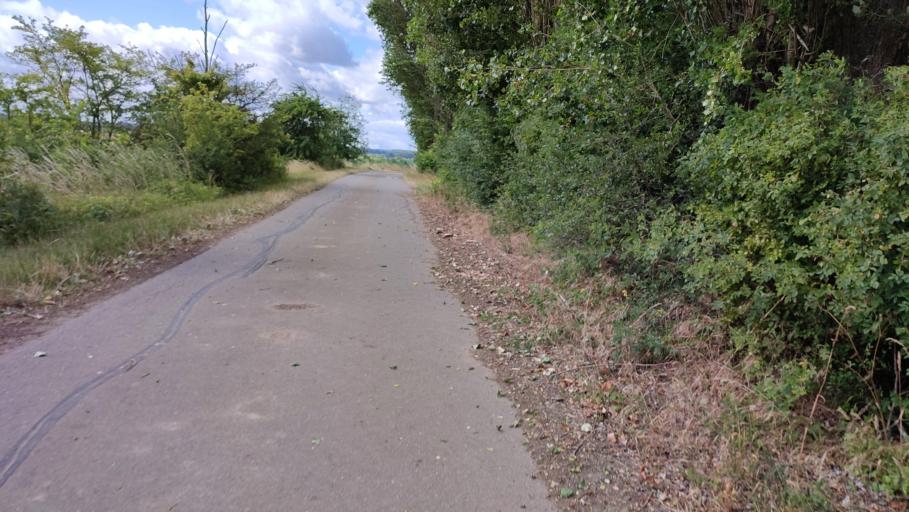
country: DE
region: Lower Saxony
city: Neu Darchau
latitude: 53.2323
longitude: 10.9644
